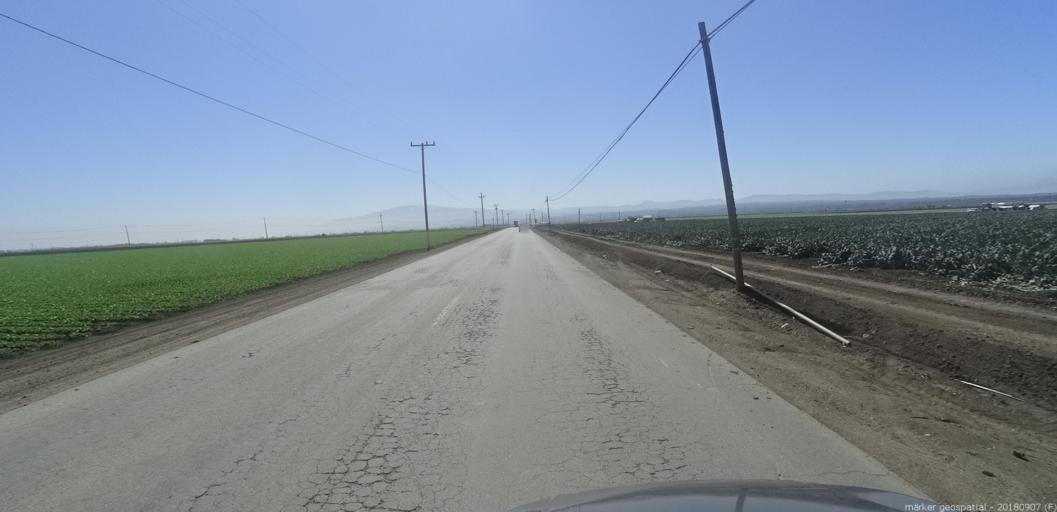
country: US
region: California
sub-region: Monterey County
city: Boronda
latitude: 36.7047
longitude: -121.7365
